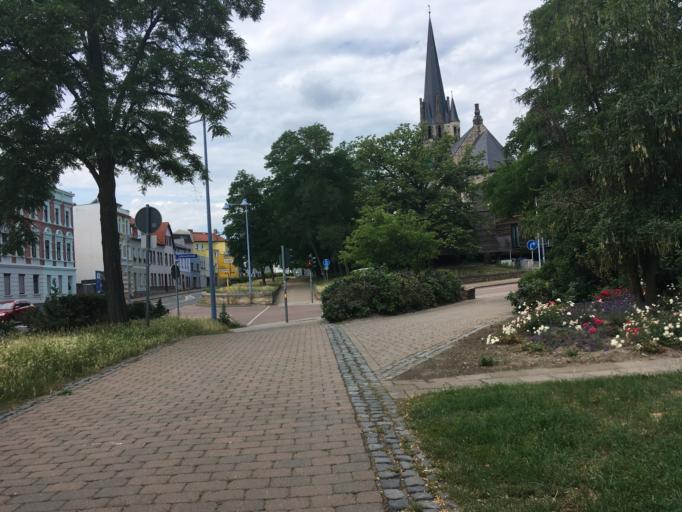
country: DE
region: Saxony-Anhalt
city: Bernburg
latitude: 51.7905
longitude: 11.7513
